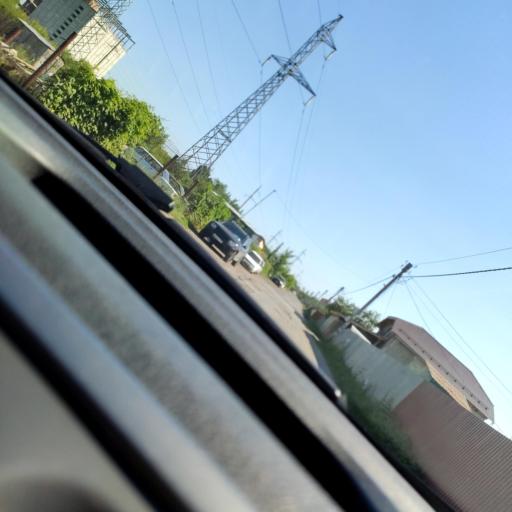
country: RU
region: Samara
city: Tol'yatti
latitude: 53.5815
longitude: 49.3000
